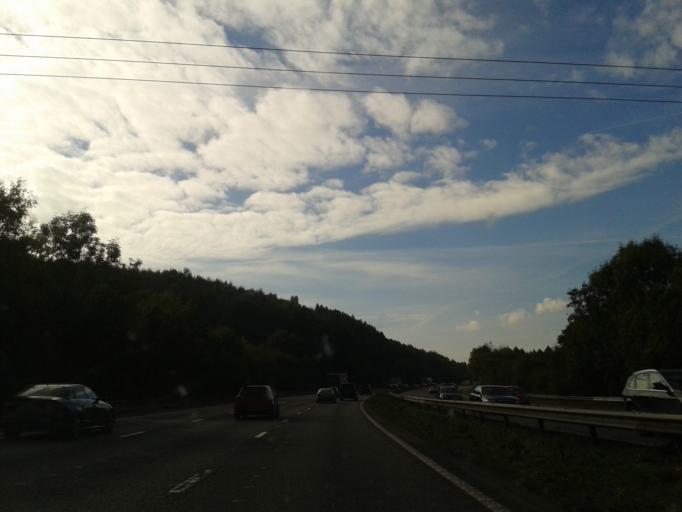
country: GB
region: England
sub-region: Staffordshire
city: Audley
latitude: 53.0210
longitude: -2.3216
